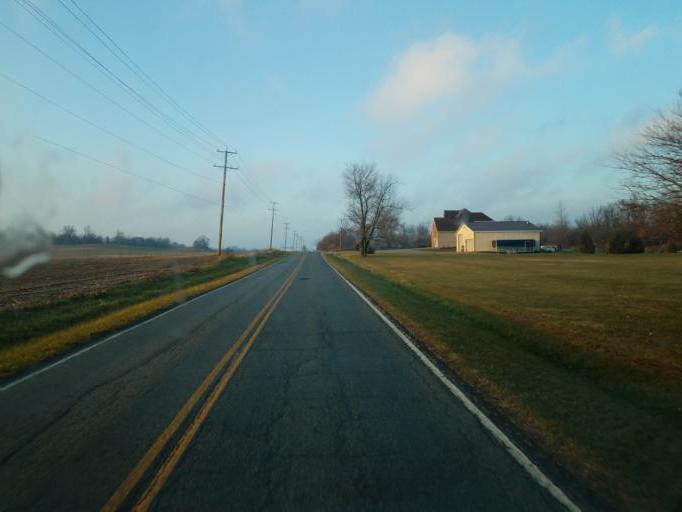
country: US
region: Ohio
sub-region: Knox County
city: Centerburg
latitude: 40.2523
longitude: -82.6931
